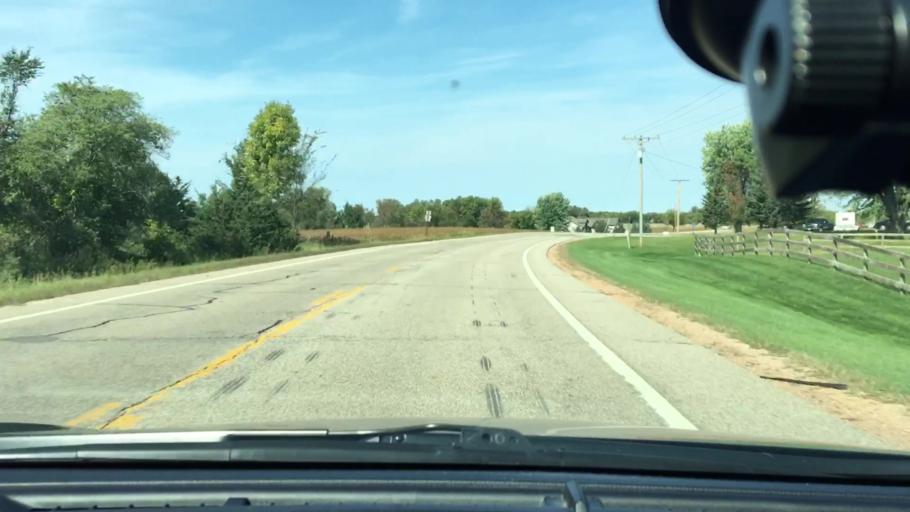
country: US
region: Minnesota
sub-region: Hennepin County
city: Corcoran
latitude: 45.1053
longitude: -93.5631
